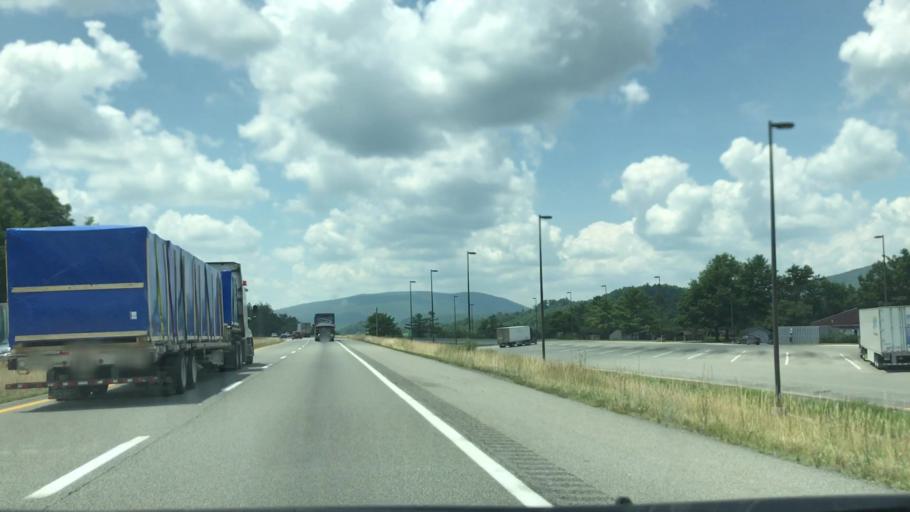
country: US
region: Virginia
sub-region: Bland County
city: Bland
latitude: 37.2065
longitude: -81.1039
